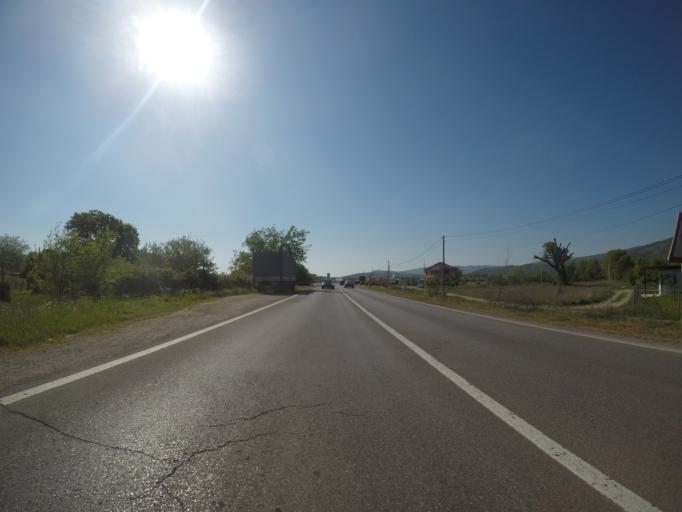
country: ME
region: Danilovgrad
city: Danilovgrad
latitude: 42.5390
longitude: 19.1115
